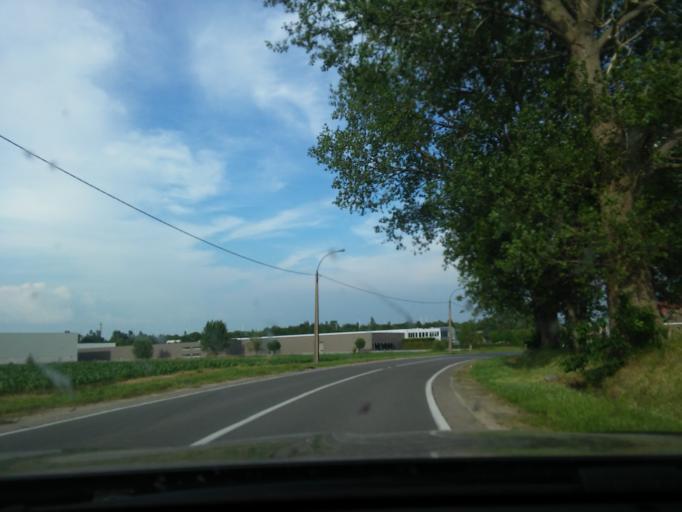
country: BE
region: Flanders
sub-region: Provincie Antwerpen
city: Kontich
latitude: 51.1221
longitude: 4.4238
